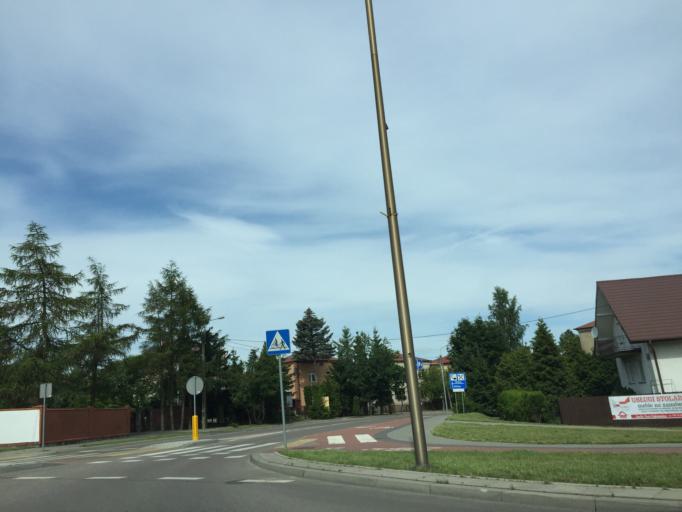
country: PL
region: Podlasie
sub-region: Suwalki
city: Suwalki
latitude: 54.0832
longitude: 22.9216
